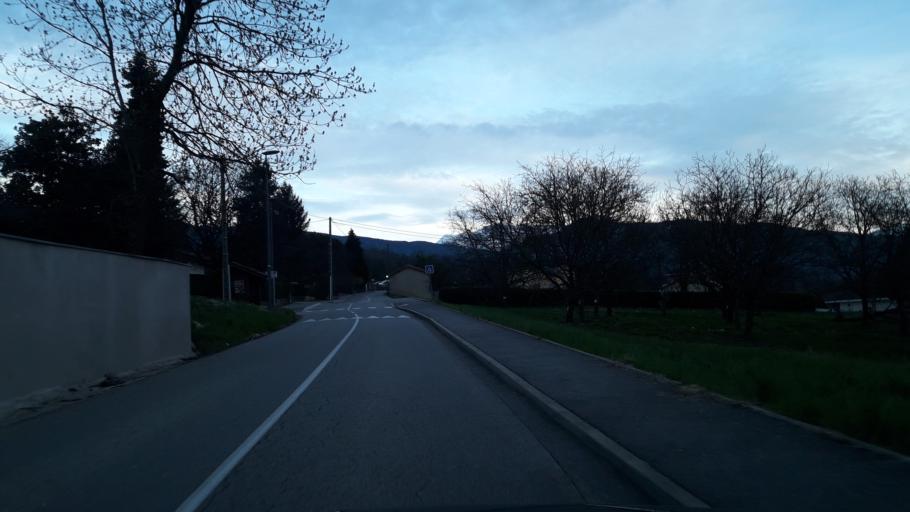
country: FR
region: Rhone-Alpes
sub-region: Departement de l'Isere
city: Brie-et-Angonnes
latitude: 45.1402
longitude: 5.7754
